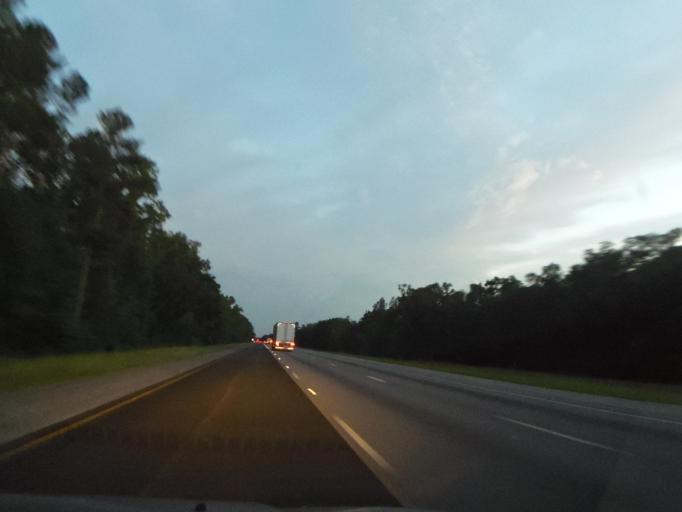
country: US
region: Georgia
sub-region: Liberty County
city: Midway
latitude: 31.7121
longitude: -81.3905
